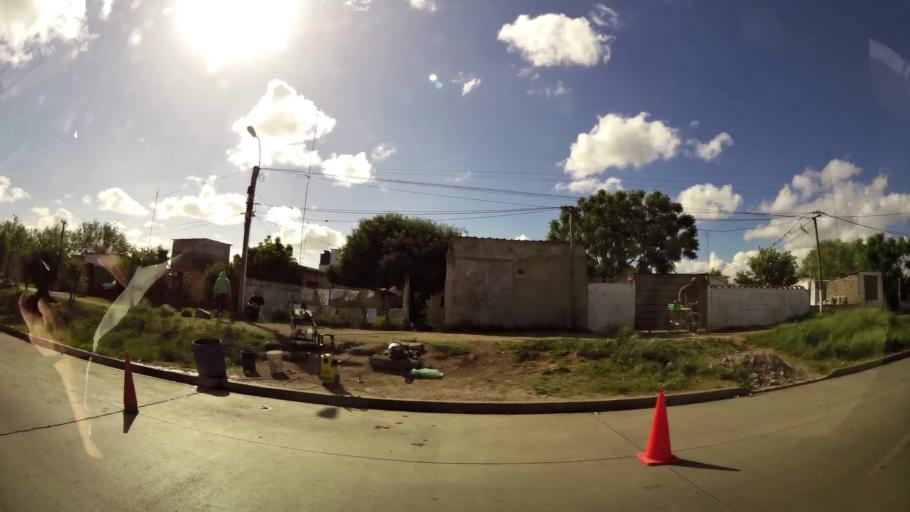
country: UY
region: Canelones
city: La Paz
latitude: -34.8147
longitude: -56.2318
